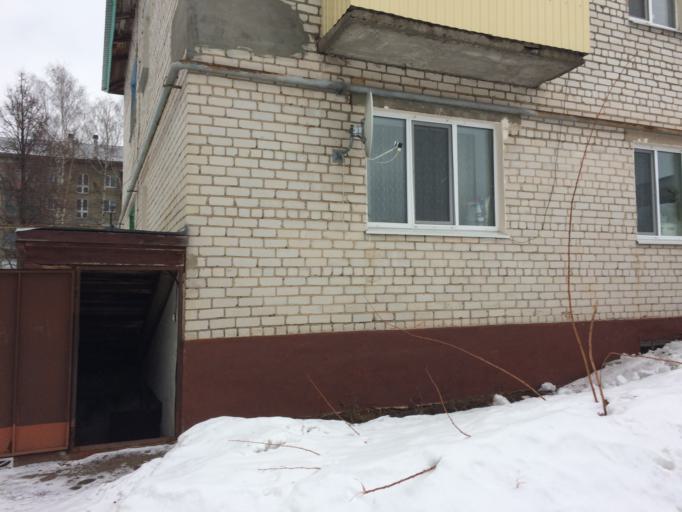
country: RU
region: Mariy-El
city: Mochalishche
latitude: 56.5444
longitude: 48.4015
